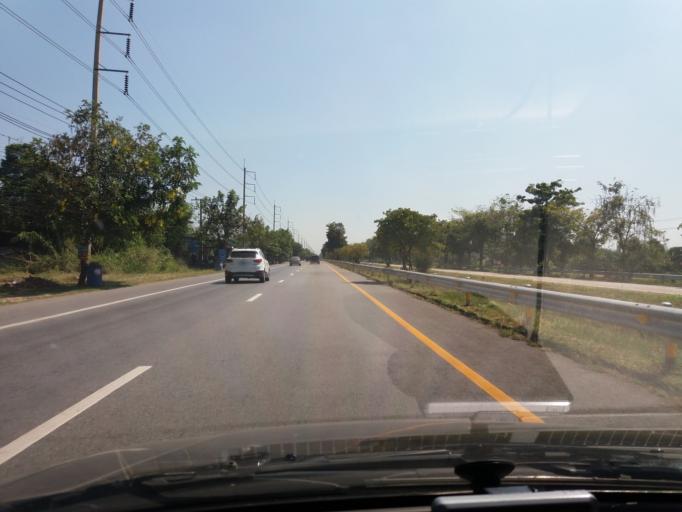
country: TH
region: Chai Nat
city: Chai Nat
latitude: 15.1345
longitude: 100.1448
